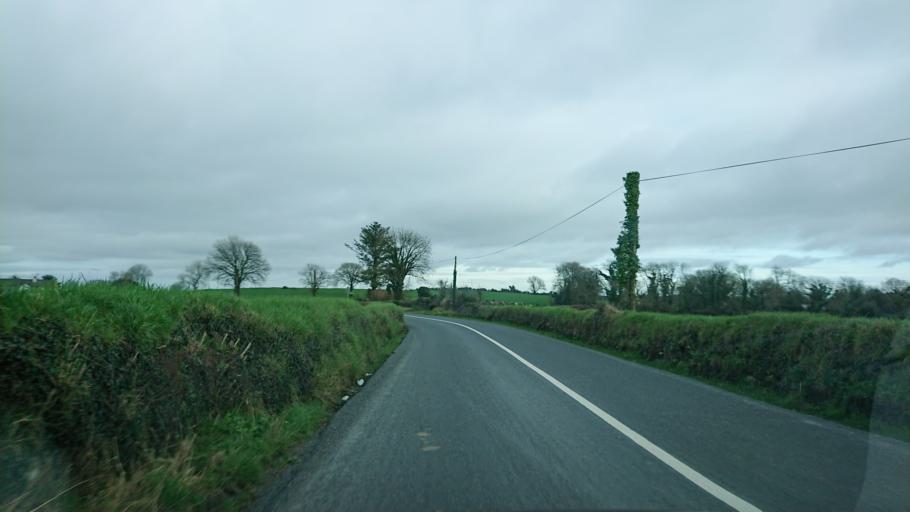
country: IE
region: Leinster
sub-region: Kilkenny
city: Mooncoin
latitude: 52.1985
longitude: -7.2684
